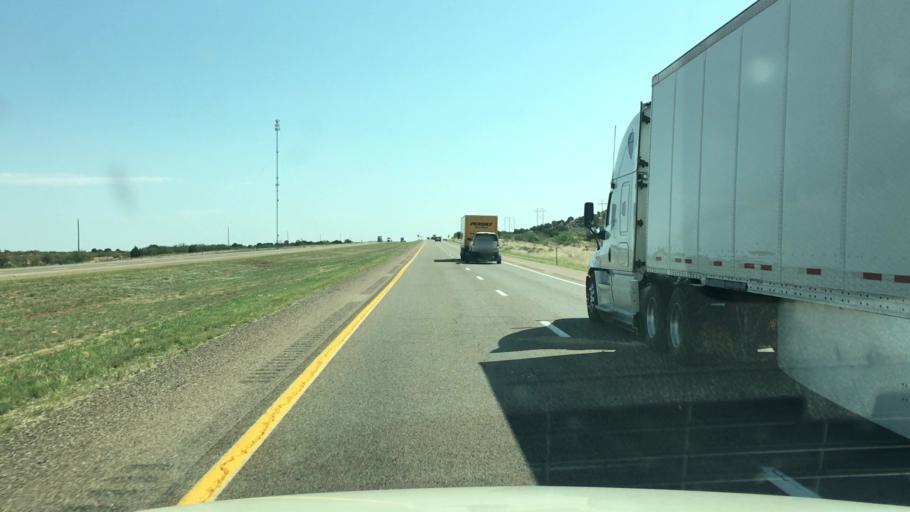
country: US
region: New Mexico
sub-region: Guadalupe County
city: Santa Rosa
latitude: 35.0427
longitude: -104.3855
